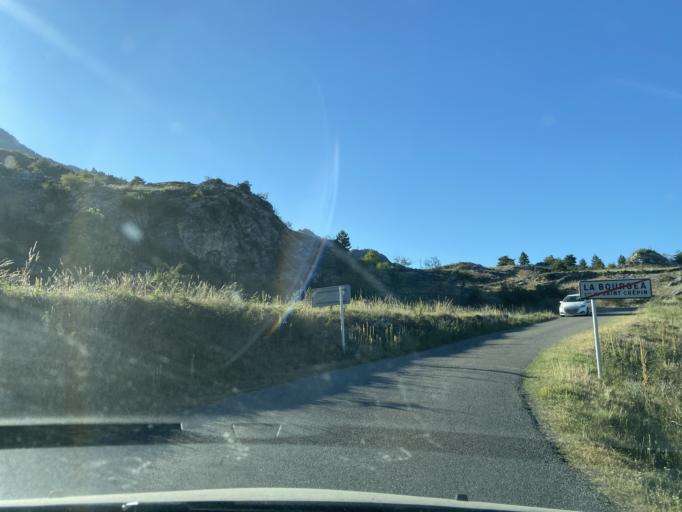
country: FR
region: Provence-Alpes-Cote d'Azur
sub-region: Departement des Hautes-Alpes
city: Guillestre
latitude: 44.7086
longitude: 6.5892
